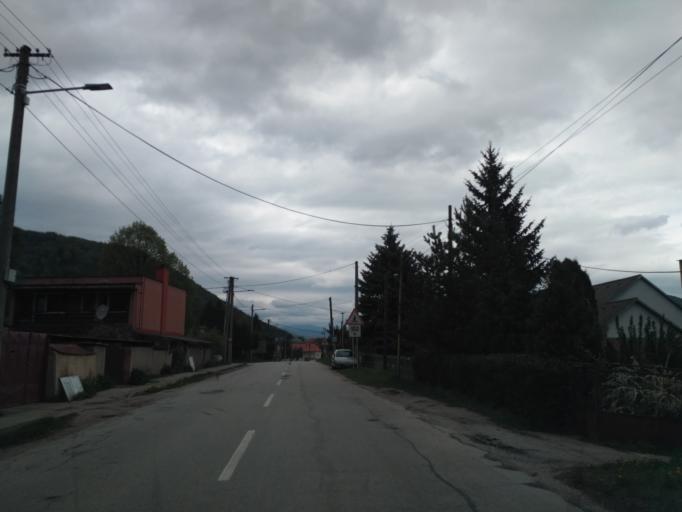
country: SK
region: Kosicky
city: Dobsina
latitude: 48.6528
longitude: 20.3664
